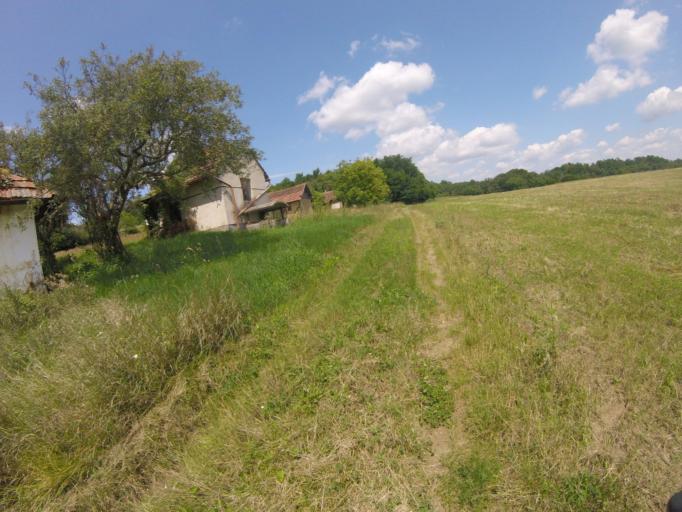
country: HU
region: Zala
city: Nagykanizsa
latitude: 46.5549
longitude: 17.0279
